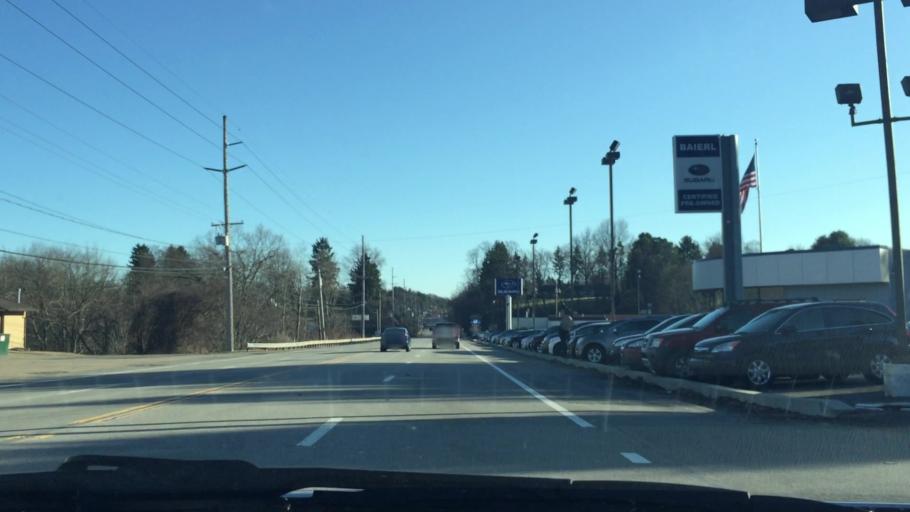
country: US
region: Pennsylvania
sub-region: Allegheny County
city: Franklin Park
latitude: 40.5800
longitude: -80.0378
